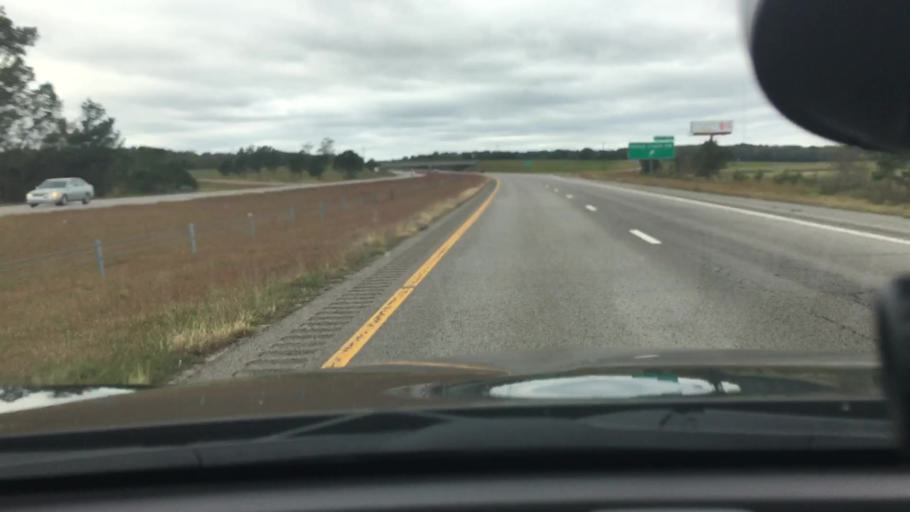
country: US
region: North Carolina
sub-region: Wilson County
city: Wilson
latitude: 35.6734
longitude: -77.9009
